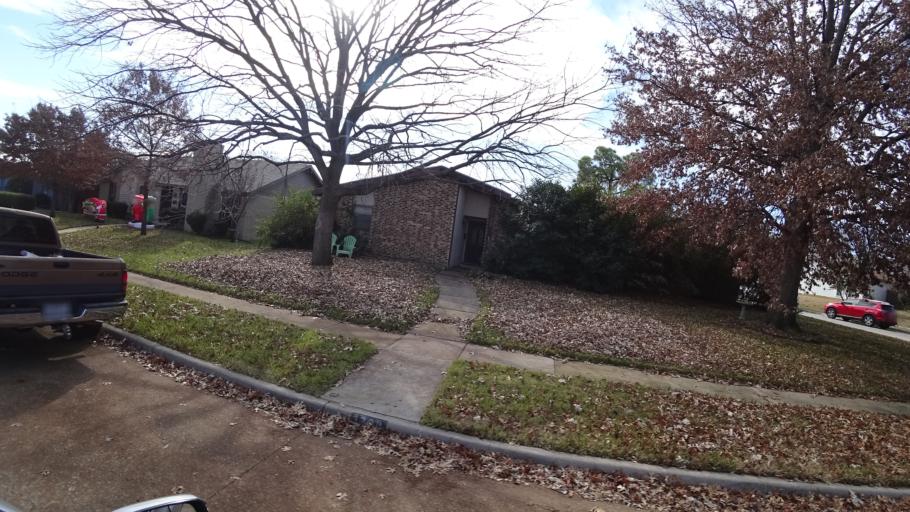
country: US
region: Texas
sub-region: Denton County
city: Lewisville
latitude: 33.0449
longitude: -97.0302
